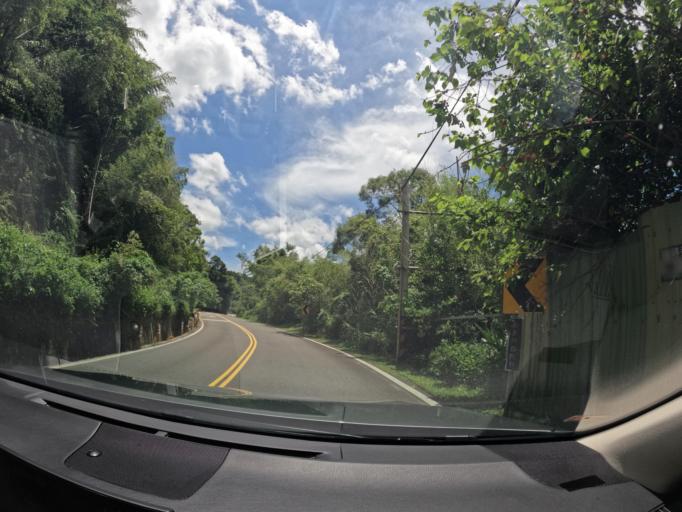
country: TW
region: Taiwan
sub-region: Hsinchu
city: Hsinchu
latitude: 24.6459
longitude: 120.9686
